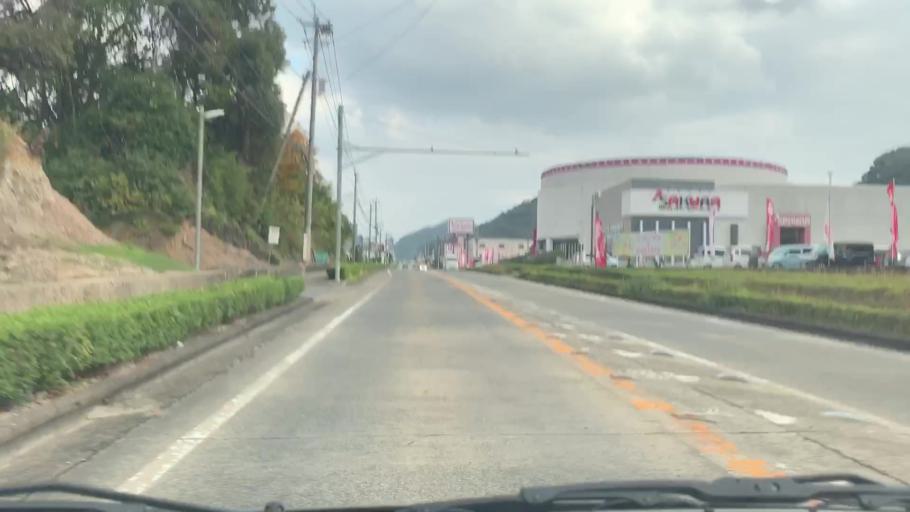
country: JP
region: Saga Prefecture
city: Imaricho-ko
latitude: 33.1860
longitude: 129.8685
